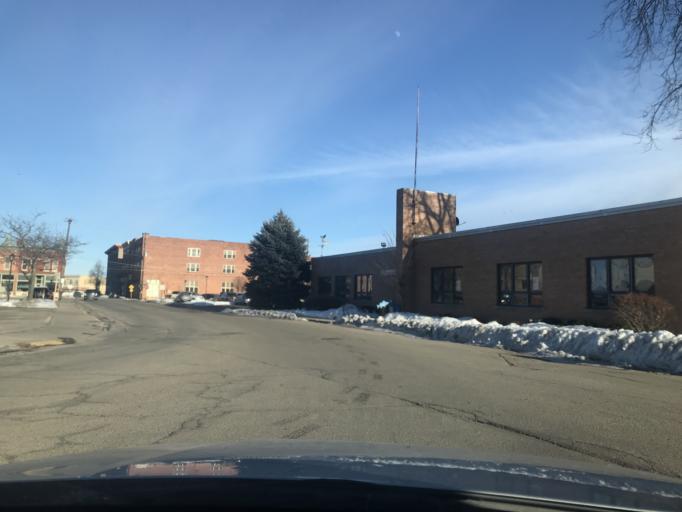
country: US
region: Wisconsin
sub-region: Marinette County
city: Marinette
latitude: 45.0988
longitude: -87.6330
